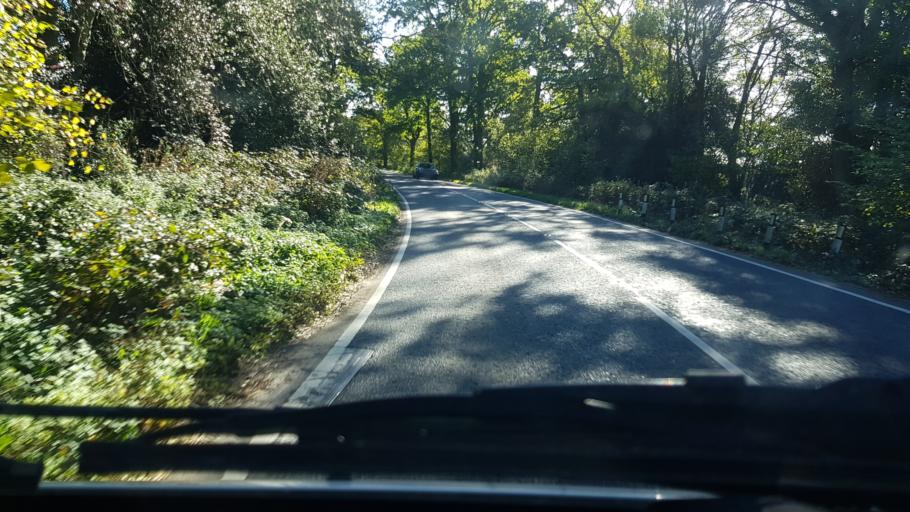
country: GB
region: England
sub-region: Surrey
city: Chilworth
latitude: 51.1764
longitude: -0.5193
